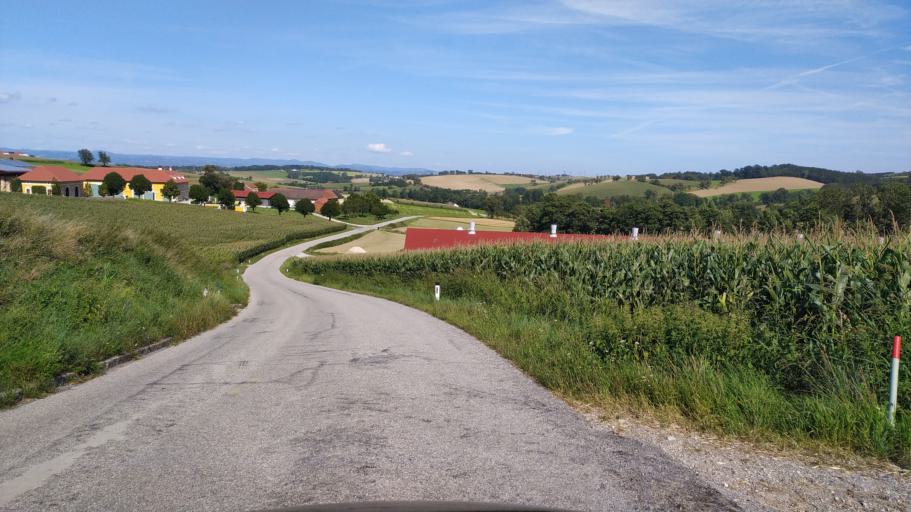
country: AT
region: Lower Austria
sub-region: Politischer Bezirk Amstetten
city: Strengberg
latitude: 48.1231
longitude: 14.6549
